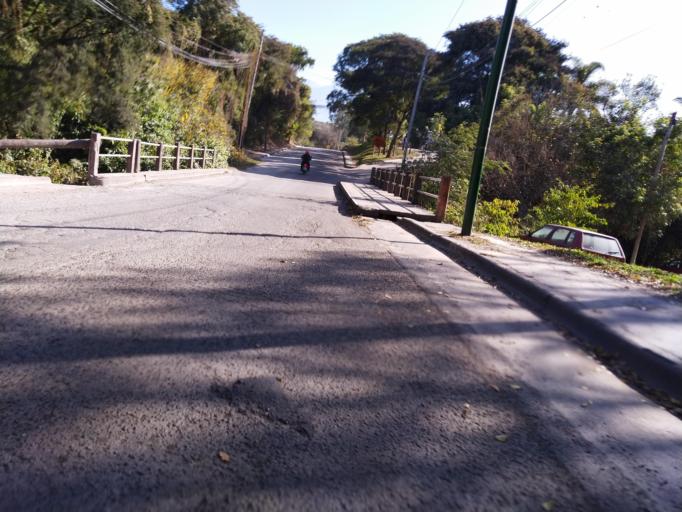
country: AR
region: Jujuy
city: San Salvador de Jujuy
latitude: -24.1793
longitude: -65.3397
